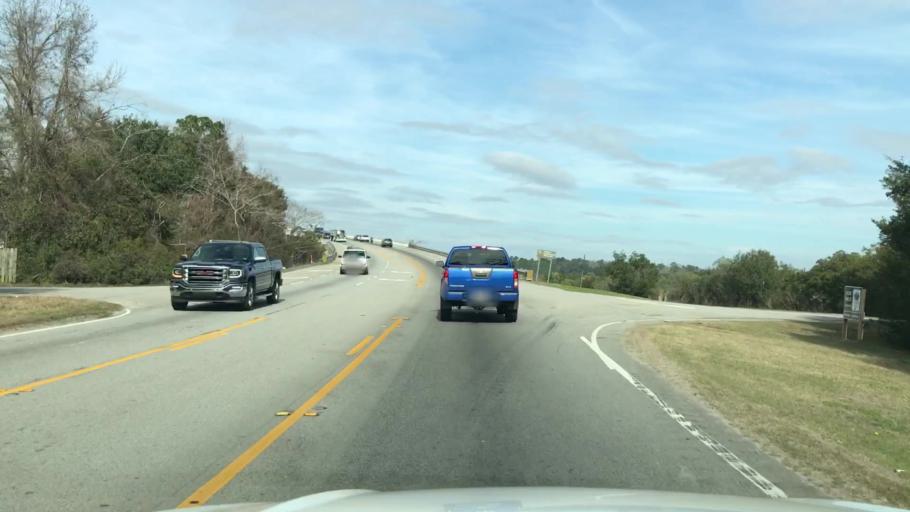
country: US
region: South Carolina
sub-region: Charleston County
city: Shell Point
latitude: 32.7800
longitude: -80.1059
